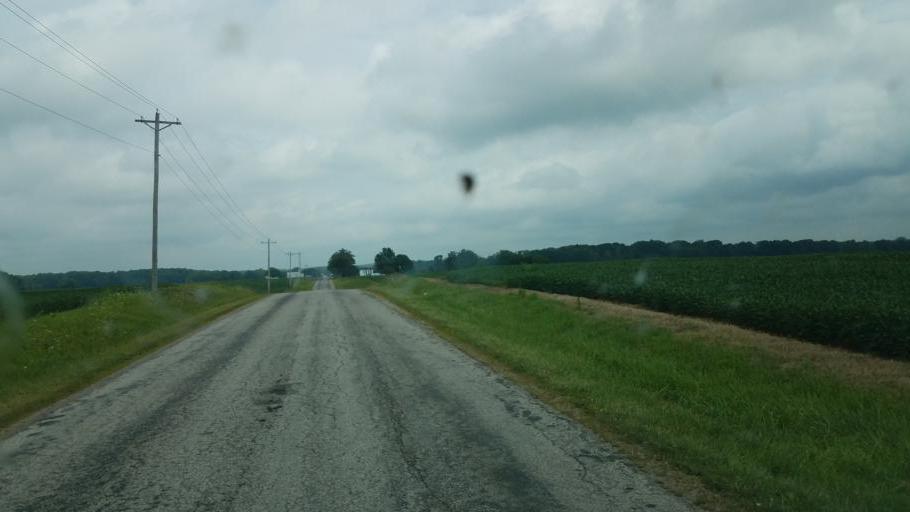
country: US
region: Ohio
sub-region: Morrow County
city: Mount Gilead
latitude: 40.4903
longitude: -82.7513
